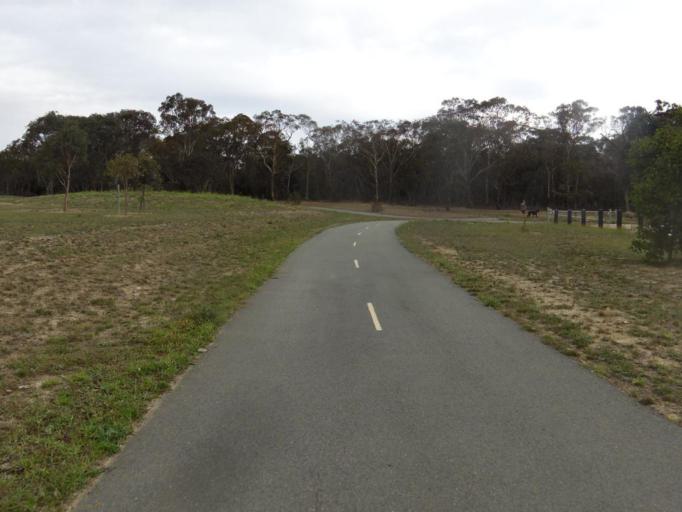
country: AU
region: Australian Capital Territory
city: Kaleen
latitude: -35.1551
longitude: 149.1552
